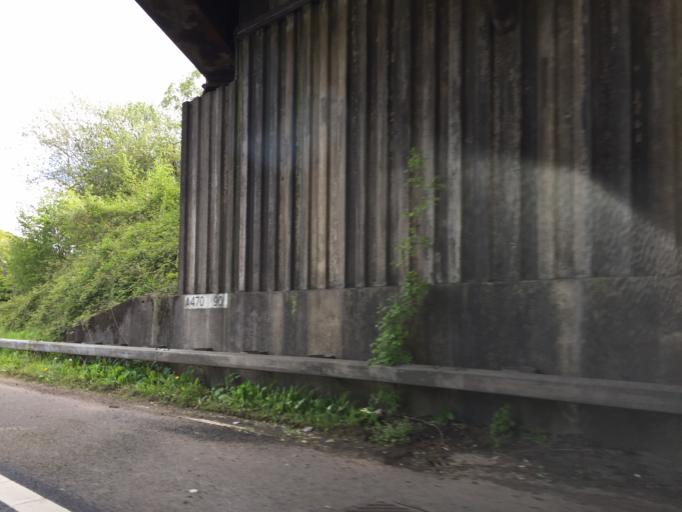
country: GB
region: Wales
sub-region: Cardiff
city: Radyr
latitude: 51.5439
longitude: -3.2633
